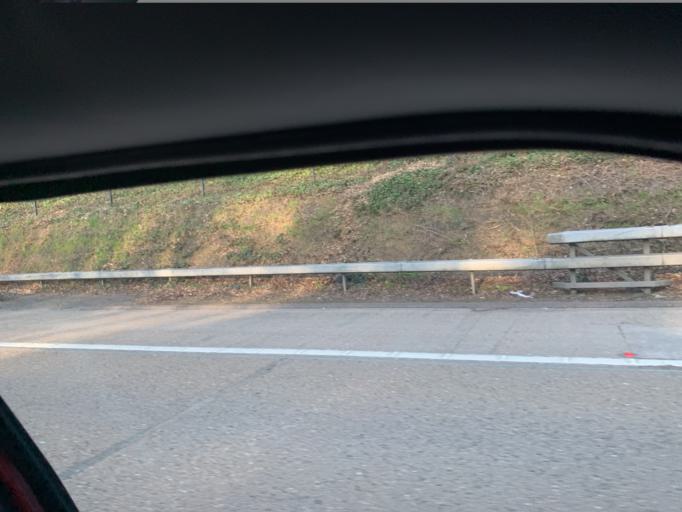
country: GB
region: England
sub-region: Surrey
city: Headley
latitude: 51.2704
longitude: -0.2534
